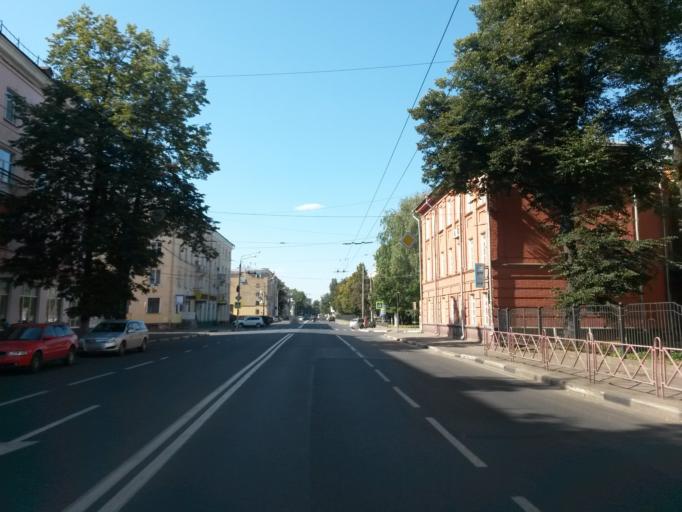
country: RU
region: Jaroslavl
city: Yaroslavl
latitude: 57.6327
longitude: 39.8866
